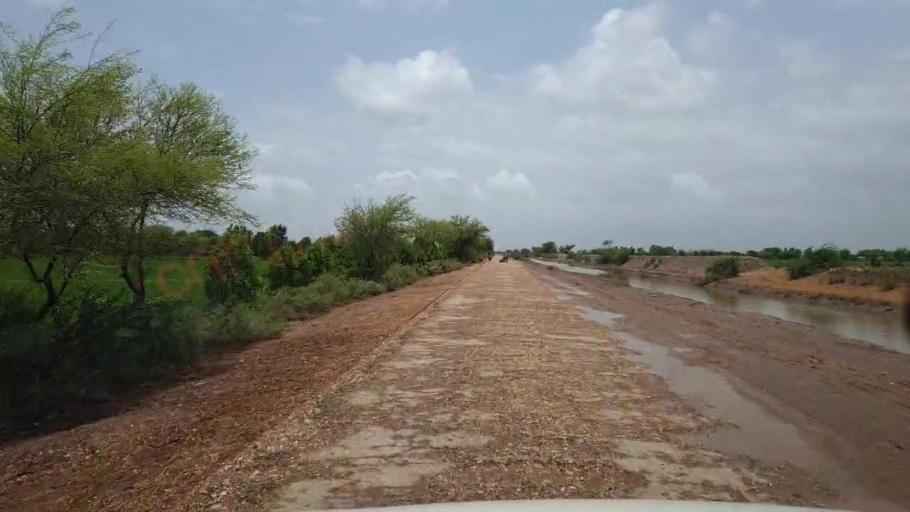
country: PK
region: Sindh
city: Kario
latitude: 24.7125
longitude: 68.5934
